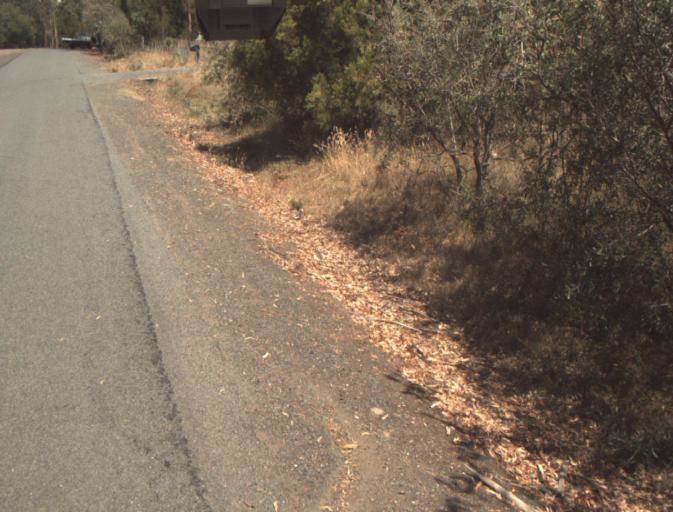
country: AU
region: Tasmania
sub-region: Launceston
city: Newstead
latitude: -41.4907
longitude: 147.1952
